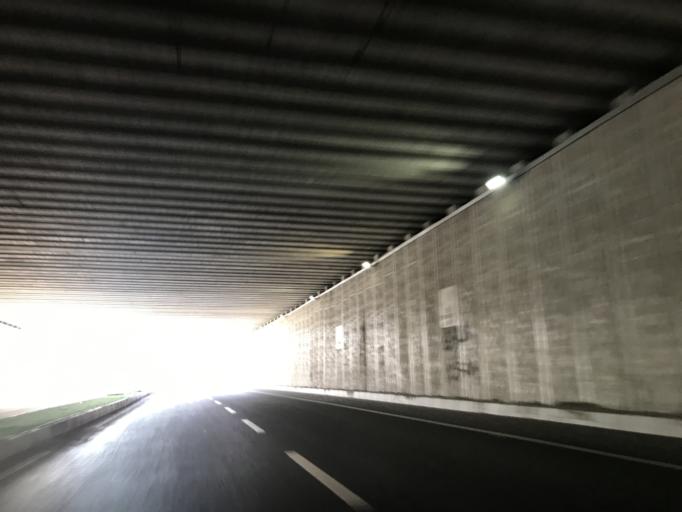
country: TR
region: Hatay
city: Iskenderun
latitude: 36.5828
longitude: 36.1684
